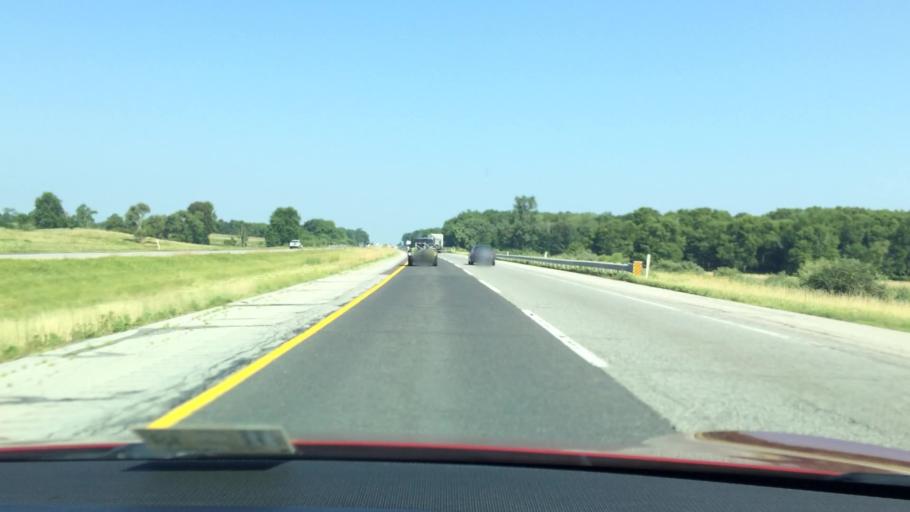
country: US
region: Indiana
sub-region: Steuben County
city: Fremont
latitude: 41.7033
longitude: -84.9227
